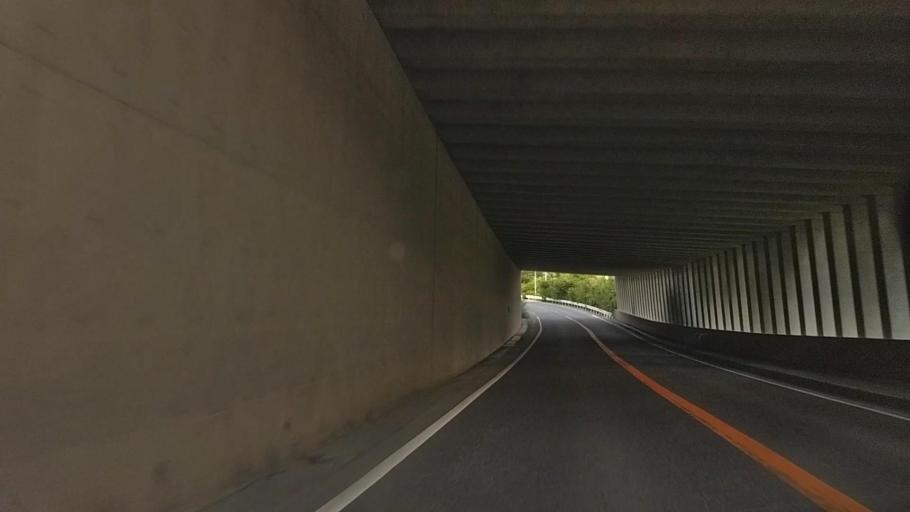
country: JP
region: Shizuoka
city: Fujinomiya
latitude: 35.3948
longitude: 138.4425
